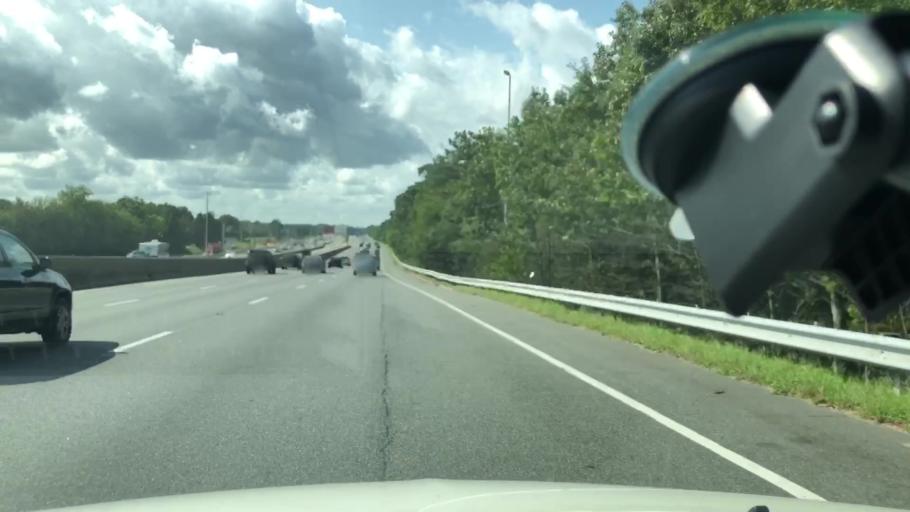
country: US
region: Virginia
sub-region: City of Chesapeake
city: Chesapeake
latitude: 36.8397
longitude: -76.1967
